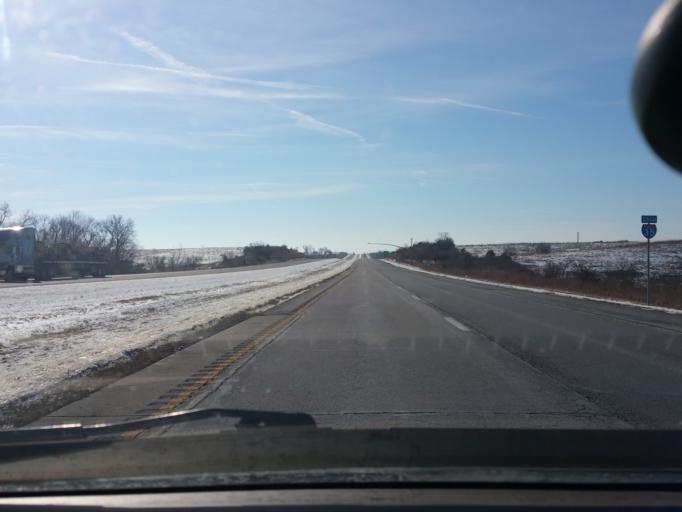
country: US
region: Iowa
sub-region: Decatur County
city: Lamoni
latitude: 40.5434
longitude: -93.9553
